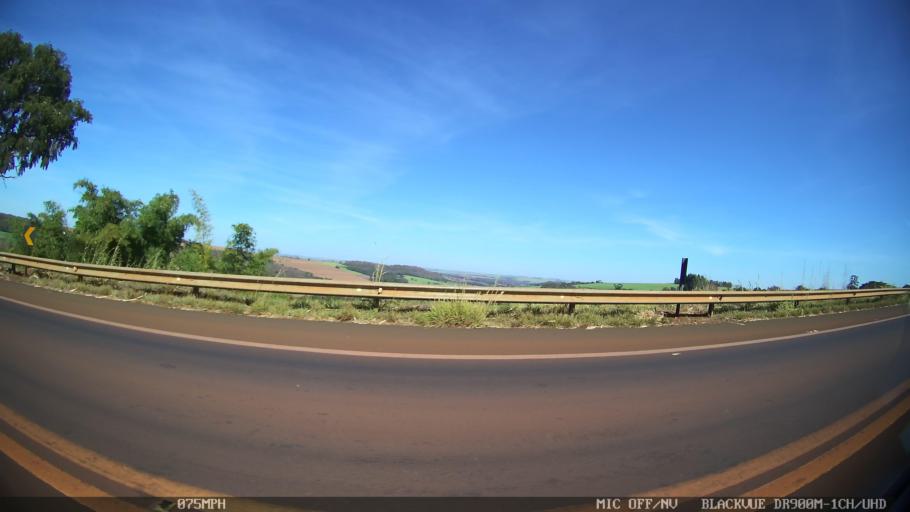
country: BR
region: Sao Paulo
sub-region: Sao Joaquim Da Barra
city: Sao Joaquim da Barra
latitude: -20.5611
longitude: -47.6895
